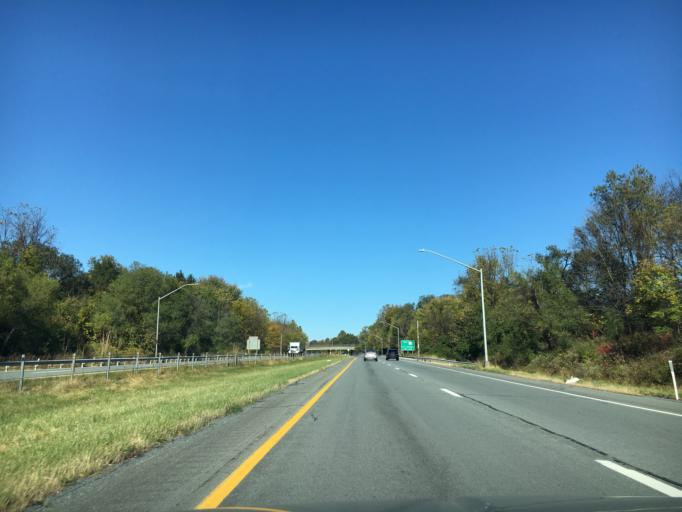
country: US
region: Pennsylvania
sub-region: Lehigh County
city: Fountain Hill
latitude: 40.6354
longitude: -75.4089
